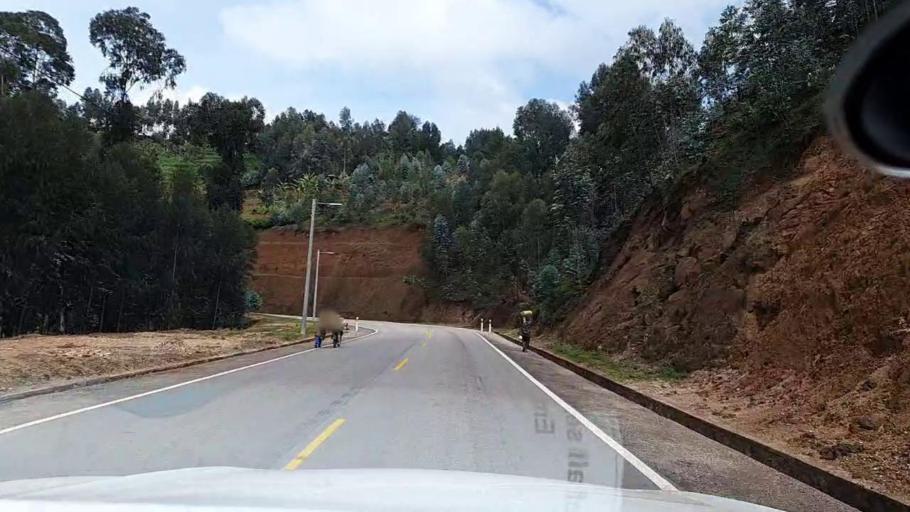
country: RW
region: Southern Province
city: Nzega
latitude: -2.5108
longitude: 29.4643
